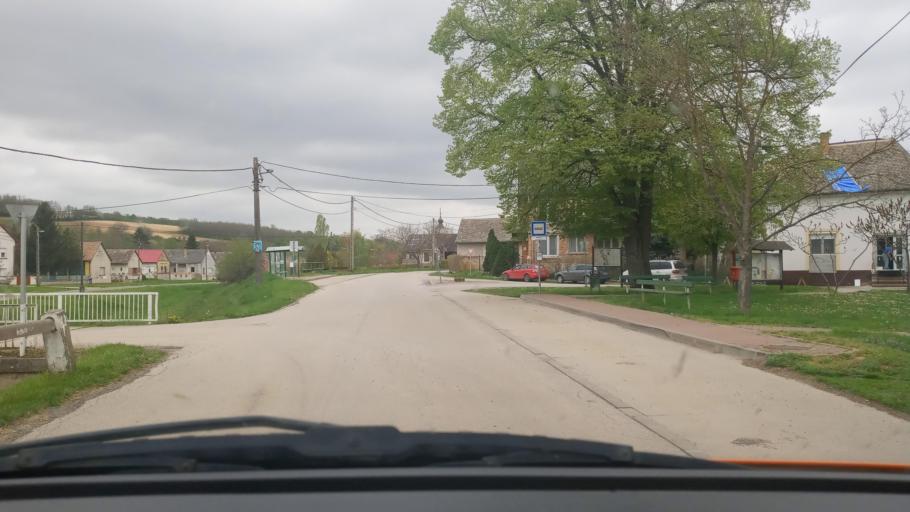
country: HU
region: Baranya
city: Boly
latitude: 46.0055
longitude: 18.5501
